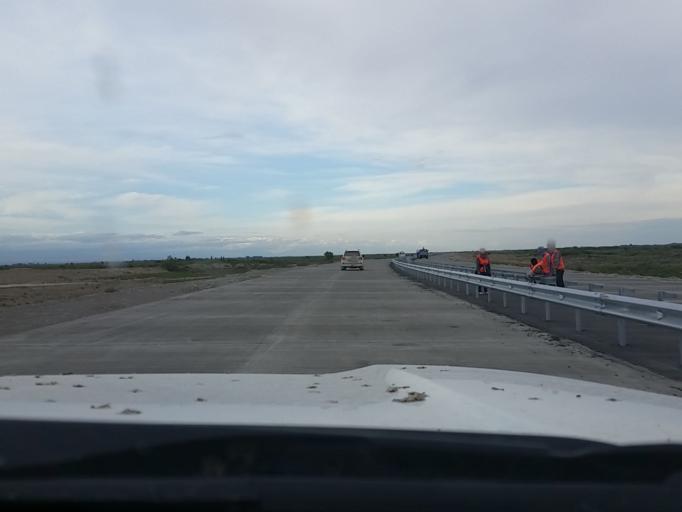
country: KZ
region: Almaty Oblysy
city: Zharkent
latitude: 44.1001
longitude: 80.0673
